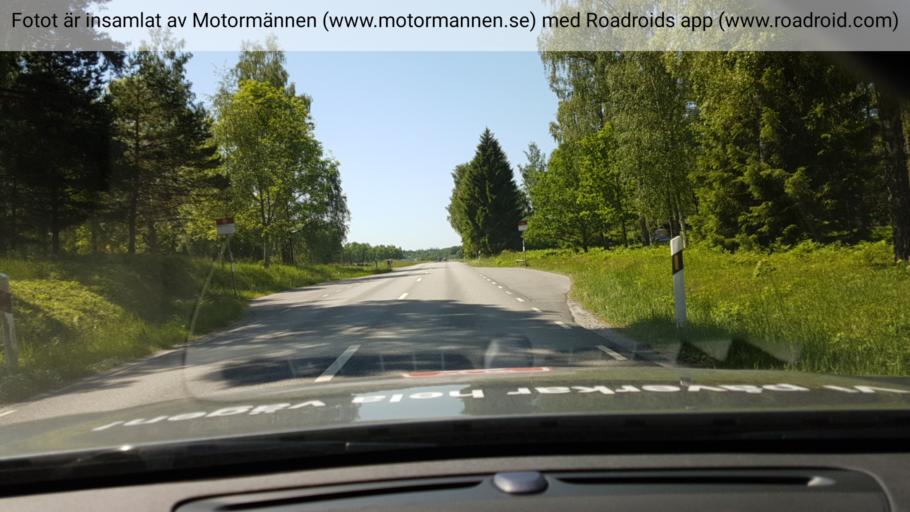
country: SE
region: Stockholm
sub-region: Norrtalje Kommun
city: Rimbo
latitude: 59.7618
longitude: 18.4064
